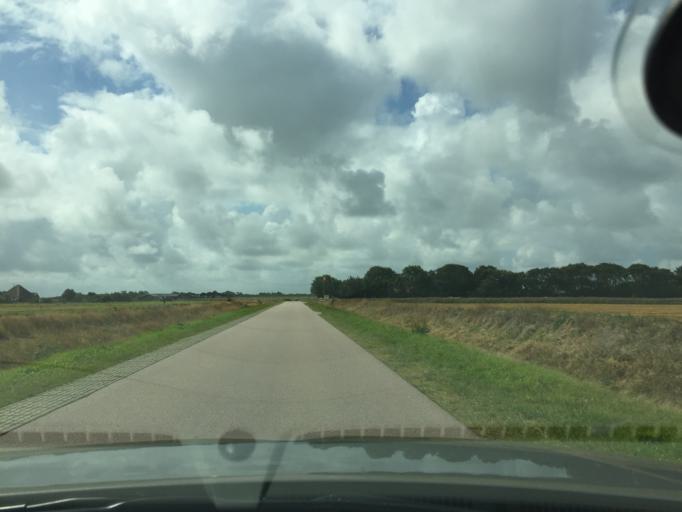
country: NL
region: North Holland
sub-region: Gemeente Texel
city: Den Burg
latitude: 53.0568
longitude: 4.7825
